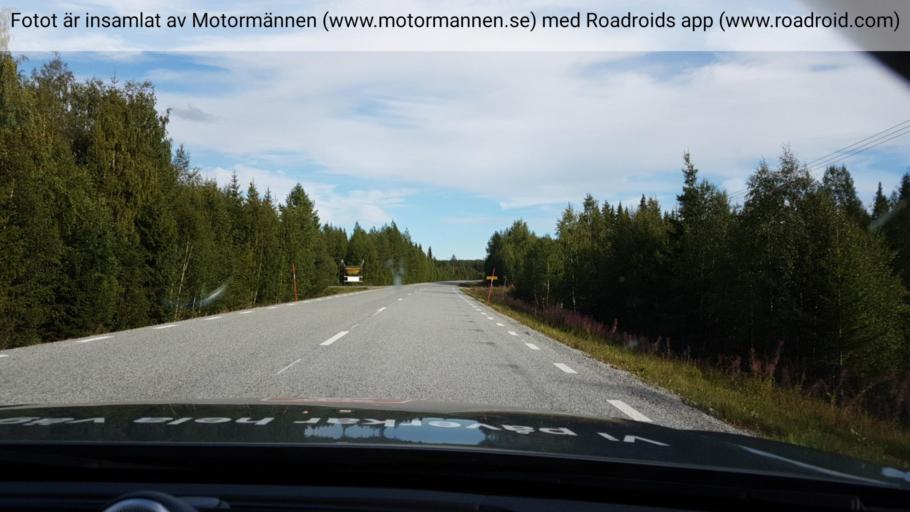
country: SE
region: Jaemtland
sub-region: Stroemsunds Kommun
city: Stroemsund
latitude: 64.2117
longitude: 15.5770
